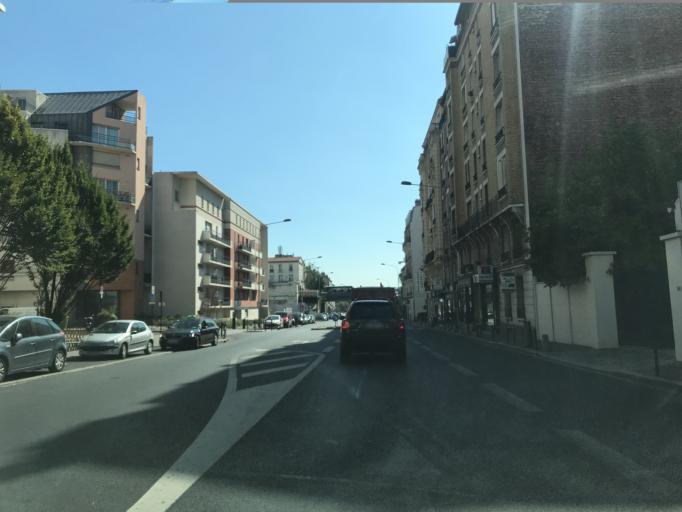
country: FR
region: Ile-de-France
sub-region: Departement des Hauts-de-Seine
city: Courbevoie
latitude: 48.8991
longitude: 2.2621
